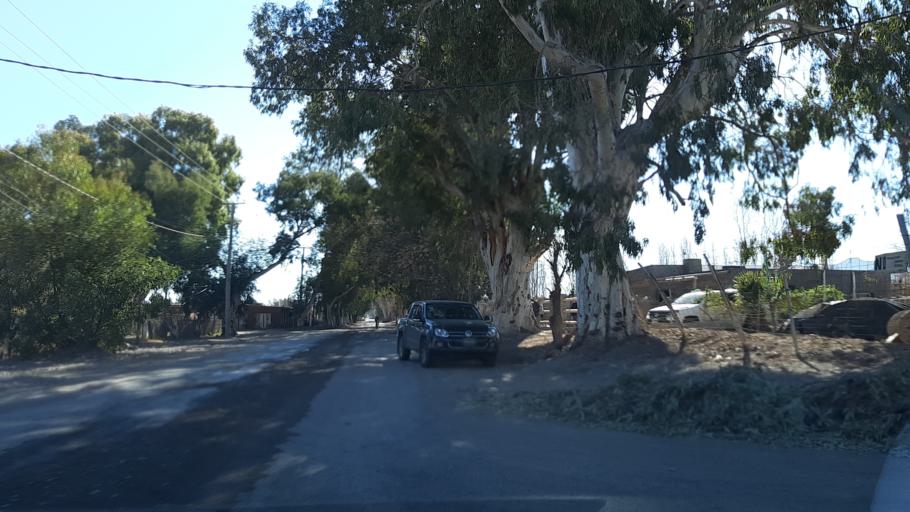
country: AR
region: San Juan
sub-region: Departamento de Zonda
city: Zonda
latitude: -31.5522
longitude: -68.7282
